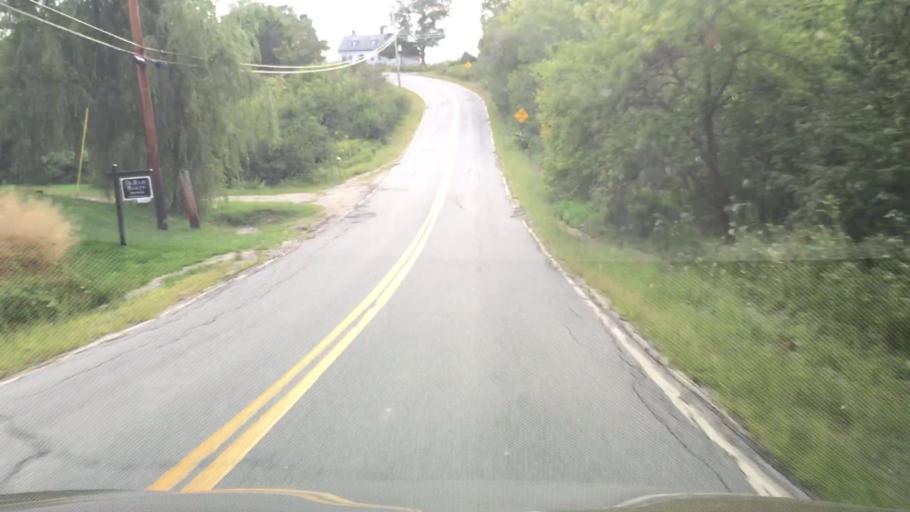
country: US
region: Maine
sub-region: Hancock County
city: Penobscot
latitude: 44.4716
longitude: -68.7367
